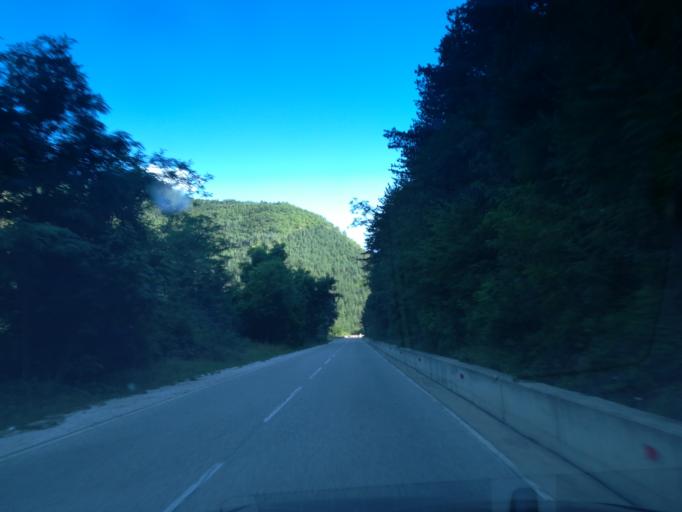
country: BG
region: Smolyan
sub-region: Obshtina Chepelare
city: Chepelare
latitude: 41.8469
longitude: 24.6805
